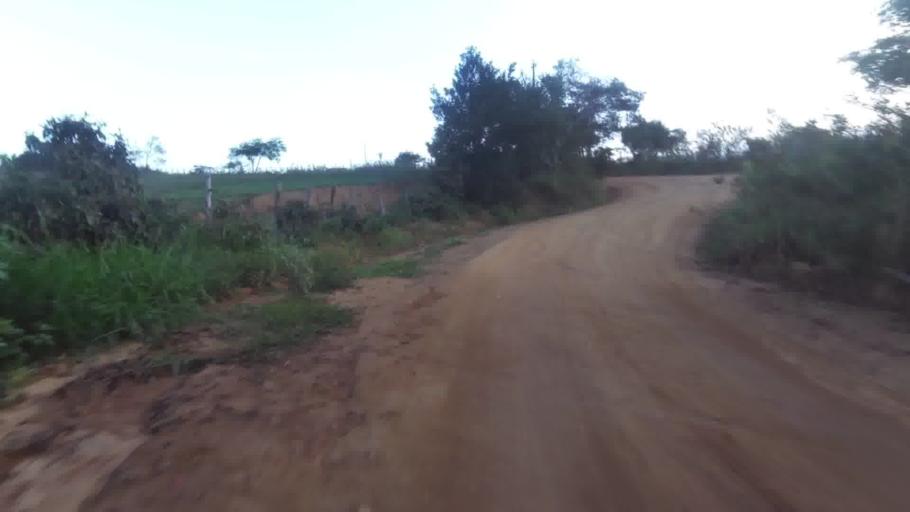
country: BR
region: Espirito Santo
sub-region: Guarapari
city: Guarapari
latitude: -20.6959
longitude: -40.5737
